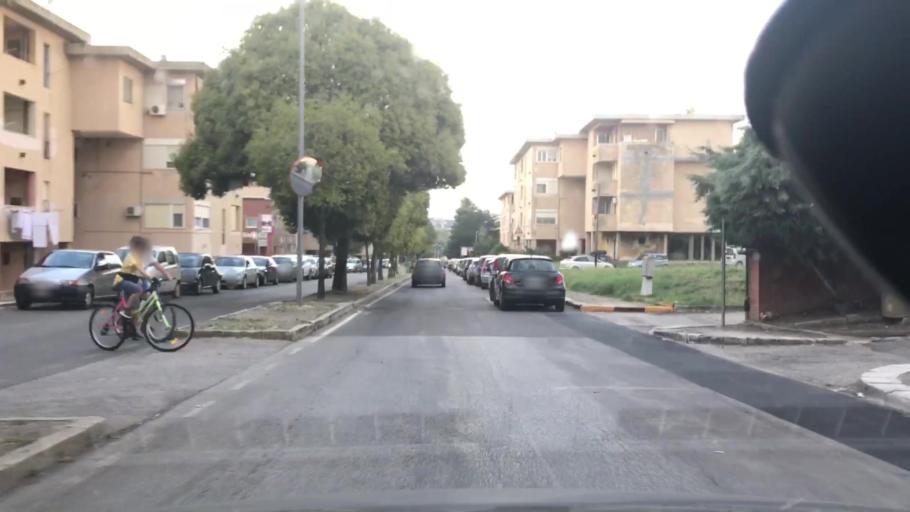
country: IT
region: Basilicate
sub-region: Provincia di Matera
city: Matera
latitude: 40.6838
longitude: 16.5847
